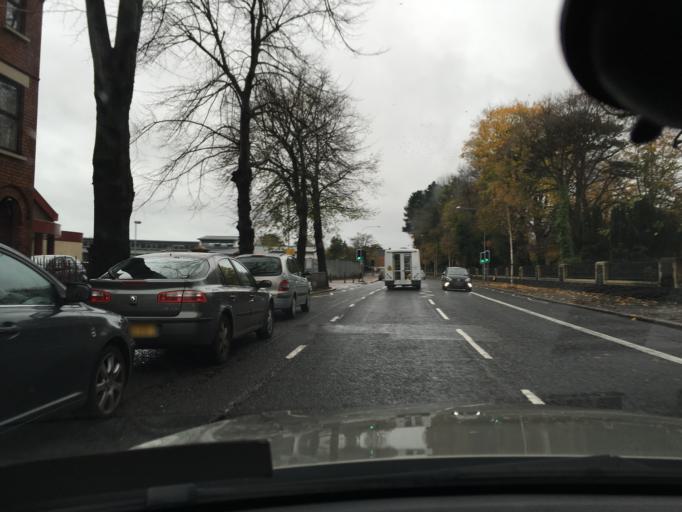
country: GB
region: Northern Ireland
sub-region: City of Belfast
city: Belfast
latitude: 54.5880
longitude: -5.9704
